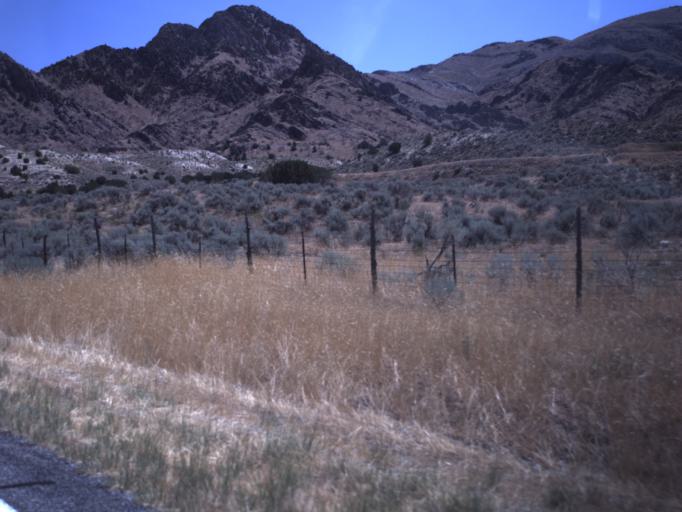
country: US
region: Utah
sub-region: Millard County
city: Delta
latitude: 39.5473
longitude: -112.2298
